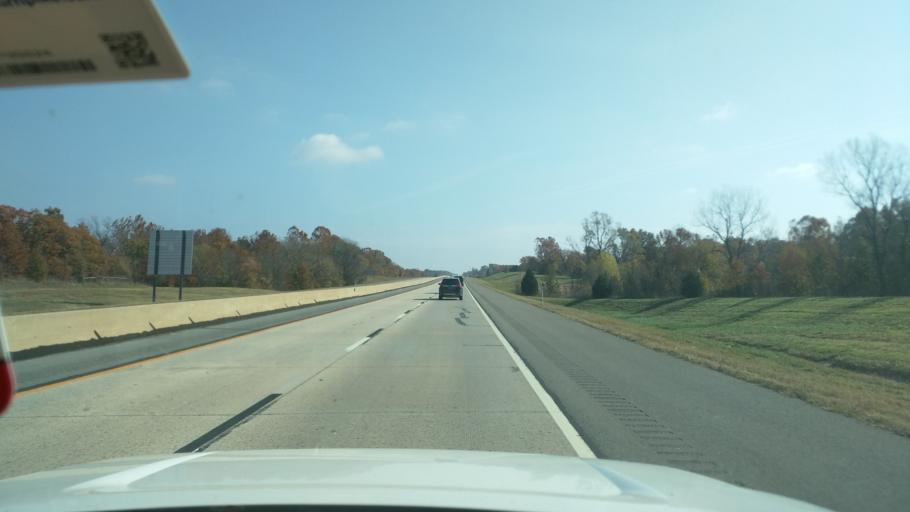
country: US
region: Oklahoma
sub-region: Muskogee County
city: Muskogee
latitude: 35.8396
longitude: -95.3886
